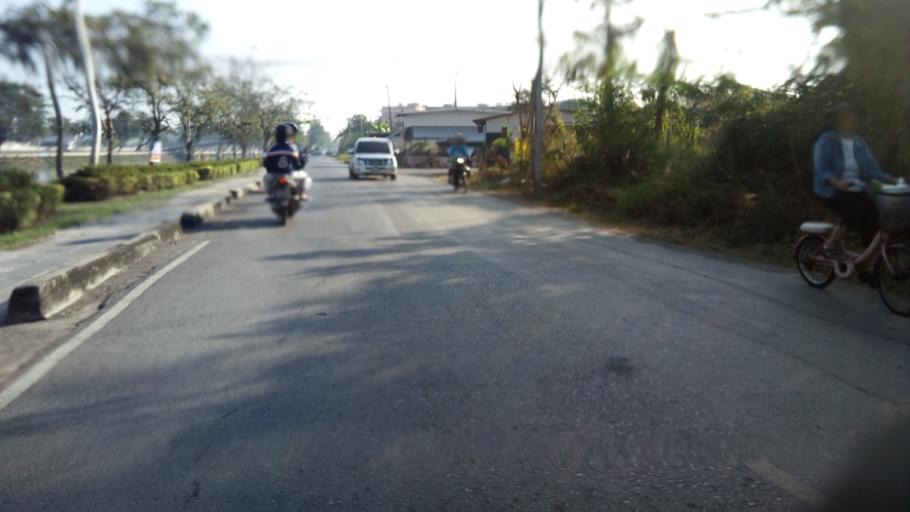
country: TH
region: Pathum Thani
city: Nong Suea
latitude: 14.0607
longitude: 100.8491
